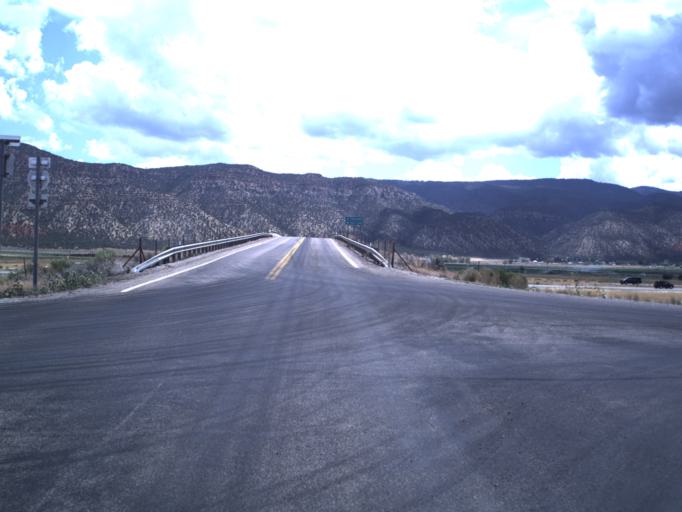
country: US
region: Utah
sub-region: Iron County
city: Parowan
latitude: 37.9101
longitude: -112.7787
